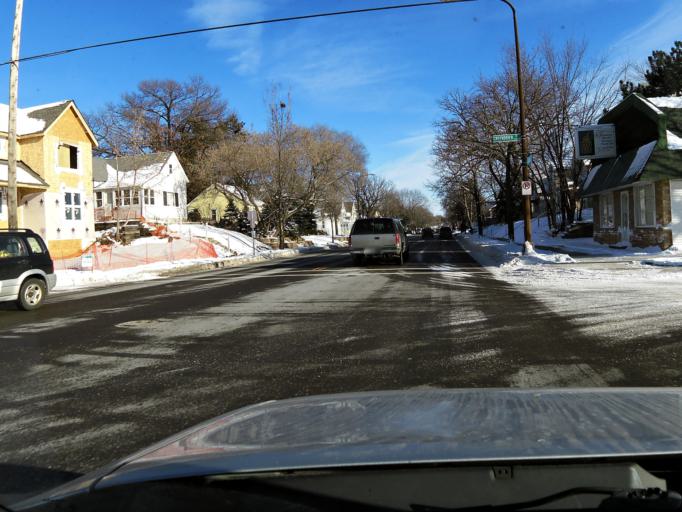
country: US
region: Minnesota
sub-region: Ramsey County
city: Saint Paul
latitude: 44.9774
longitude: -93.0712
